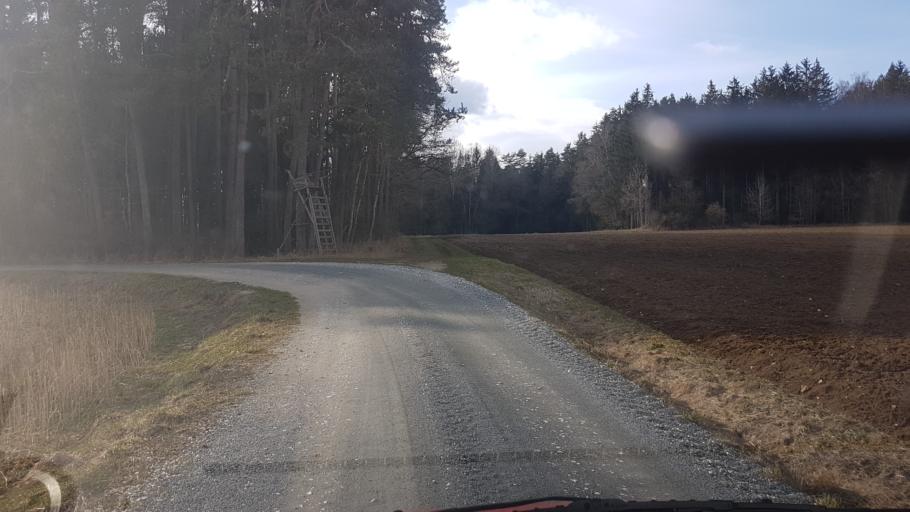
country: DE
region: Bavaria
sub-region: Upper Franconia
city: Stadelhofen
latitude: 50.0007
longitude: 11.2297
